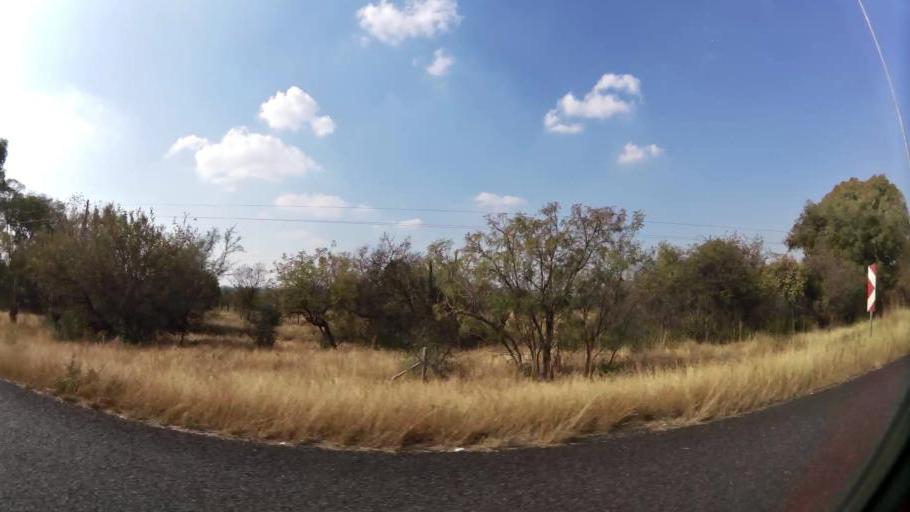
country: ZA
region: North-West
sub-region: Bojanala Platinum District Municipality
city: Rustenburg
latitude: -25.6229
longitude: 27.1568
